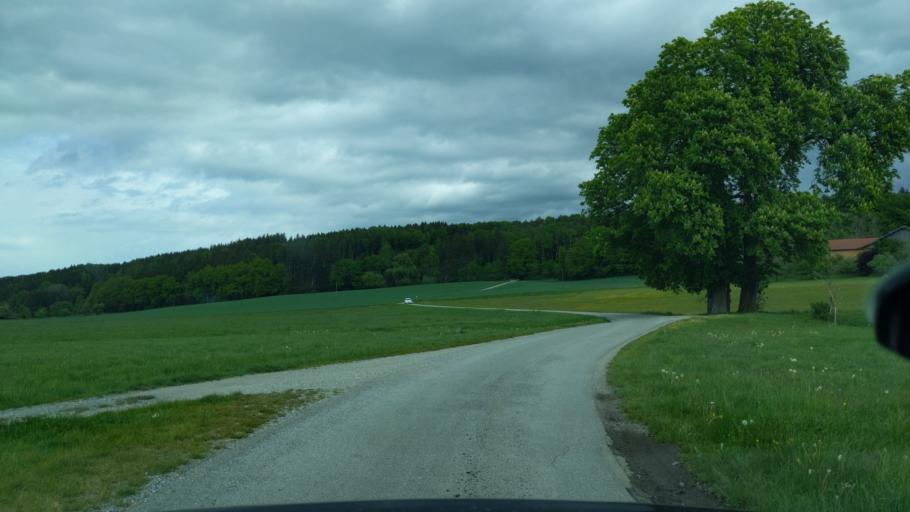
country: DE
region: Bavaria
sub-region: Upper Bavaria
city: Grafing bei Munchen
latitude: 48.0580
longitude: 11.9808
